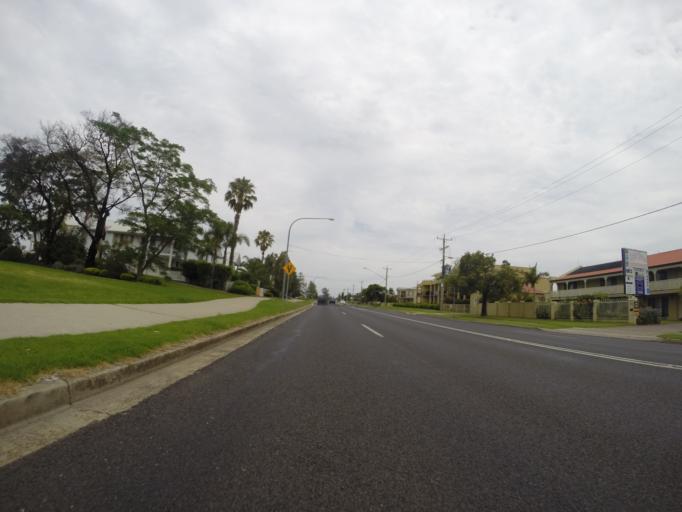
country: AU
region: New South Wales
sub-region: Eurobodalla
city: Batemans Bay
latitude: -35.7114
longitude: 150.1832
